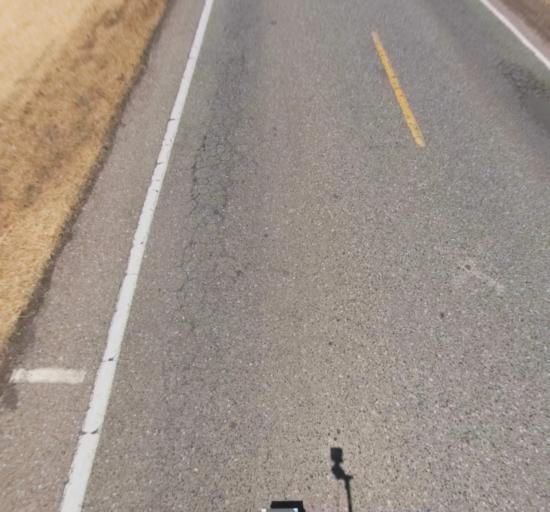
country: US
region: California
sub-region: Madera County
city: Madera Acres
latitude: 36.9965
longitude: -120.1189
